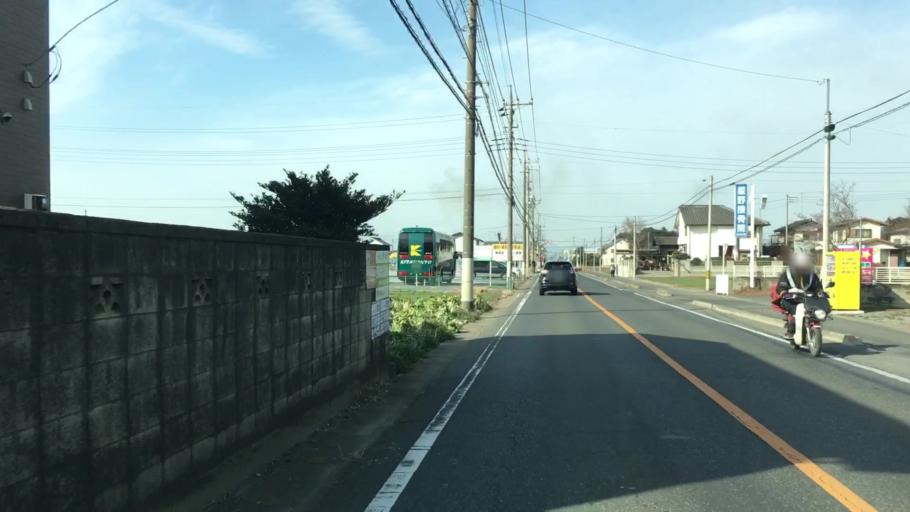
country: JP
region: Saitama
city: Menuma
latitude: 36.2400
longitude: 139.4558
